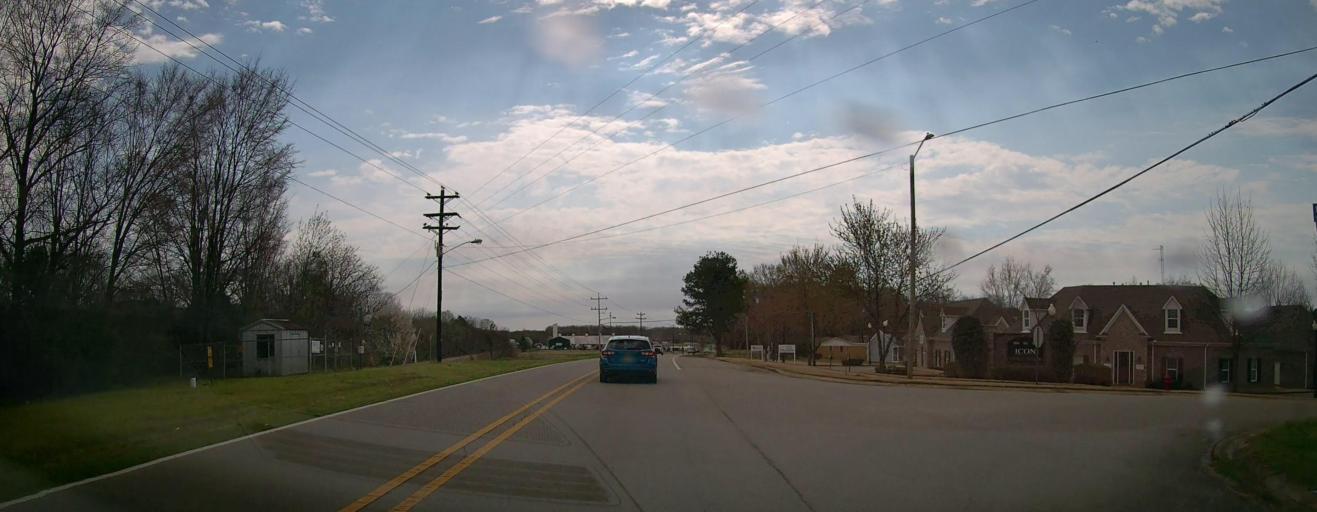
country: US
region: Mississippi
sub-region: De Soto County
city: Olive Branch
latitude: 34.9550
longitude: -89.8161
